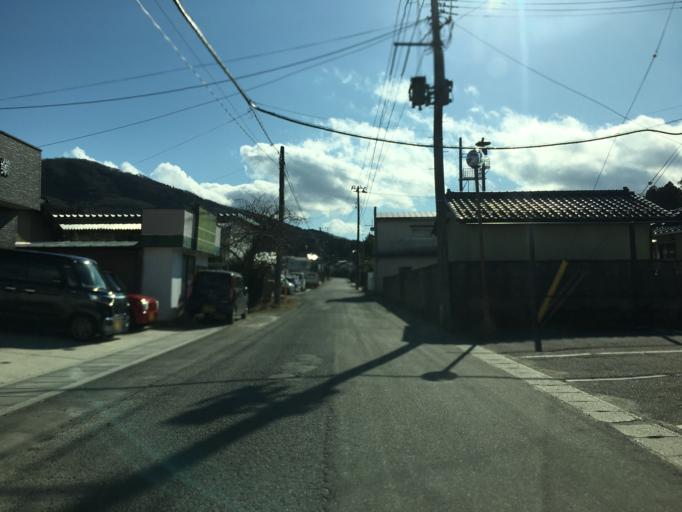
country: JP
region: Fukushima
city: Funehikimachi-funehiki
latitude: 37.4398
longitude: 140.5630
